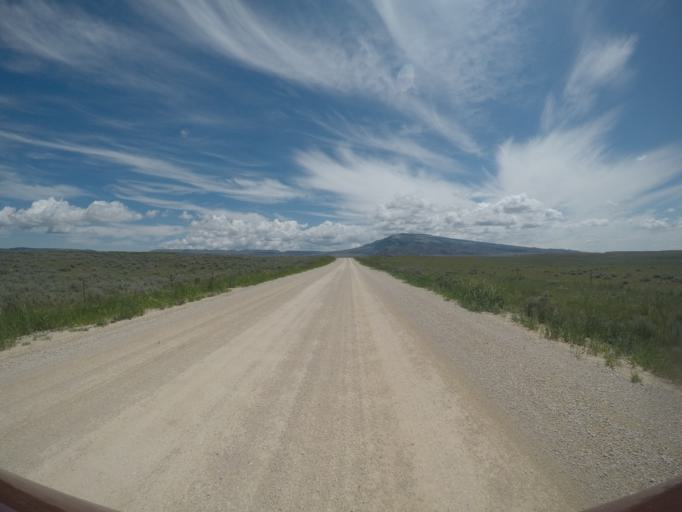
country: US
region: Wyoming
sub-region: Park County
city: Powell
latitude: 45.2050
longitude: -108.7426
